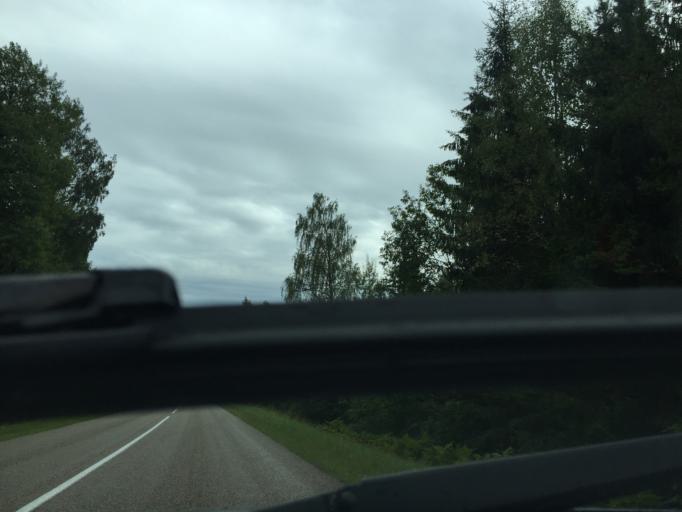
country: LV
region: Dagda
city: Dagda
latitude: 56.1842
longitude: 27.3752
